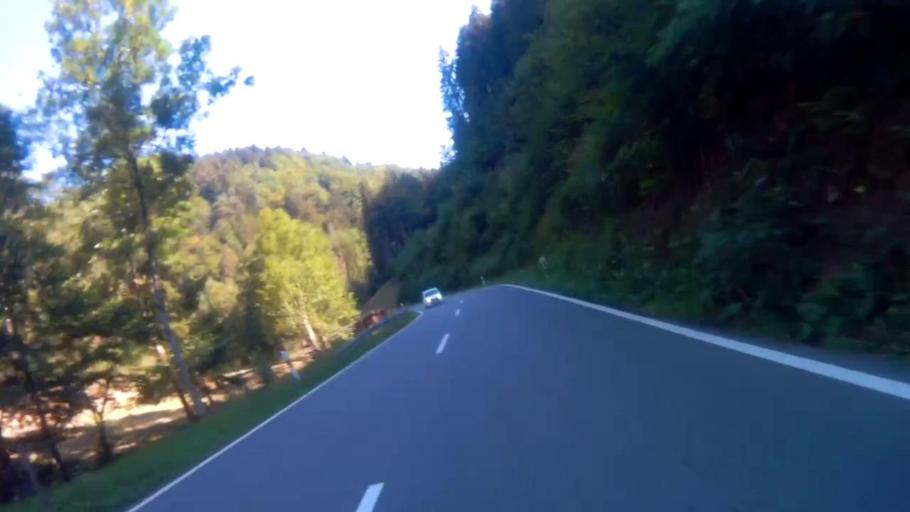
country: DE
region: Baden-Wuerttemberg
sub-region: Freiburg Region
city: Zell im Wiesental
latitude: 47.7345
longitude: 7.7697
